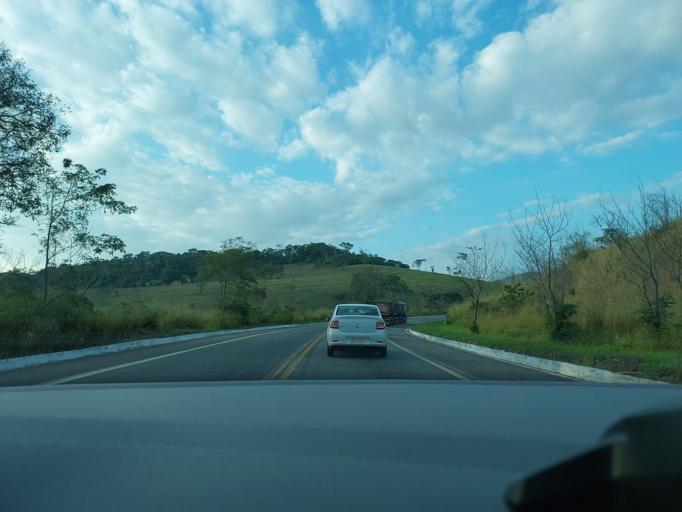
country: BR
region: Minas Gerais
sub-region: Muriae
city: Muriae
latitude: -21.1263
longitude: -42.2735
